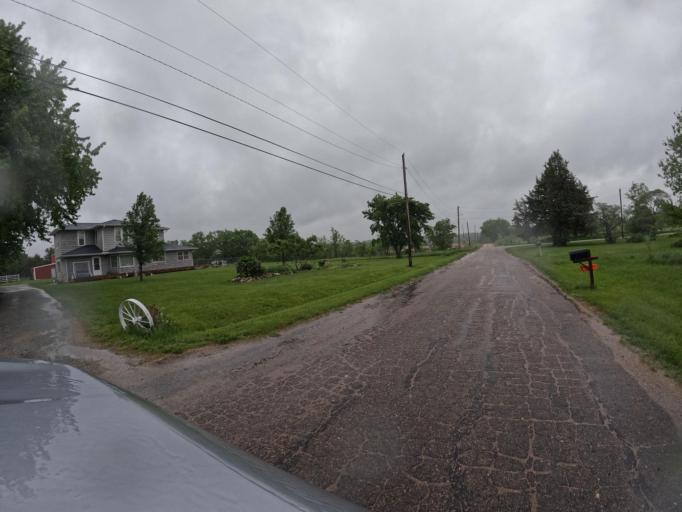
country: US
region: Nebraska
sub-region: Gage County
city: Wymore
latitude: 40.1277
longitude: -96.6566
